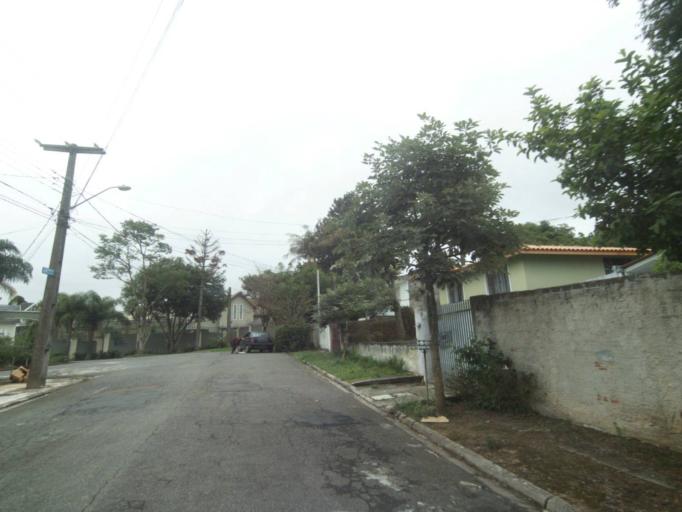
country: BR
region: Parana
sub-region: Curitiba
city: Curitiba
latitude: -25.4253
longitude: -49.3447
